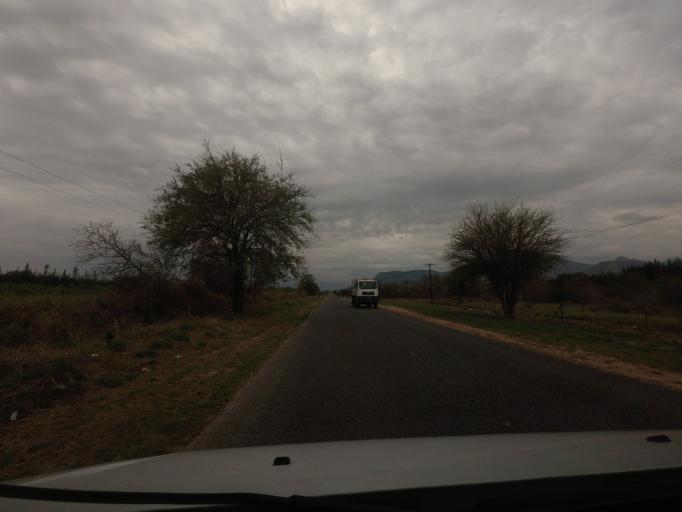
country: ZA
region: Limpopo
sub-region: Mopani District Municipality
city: Hoedspruit
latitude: -24.4556
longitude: 30.8655
